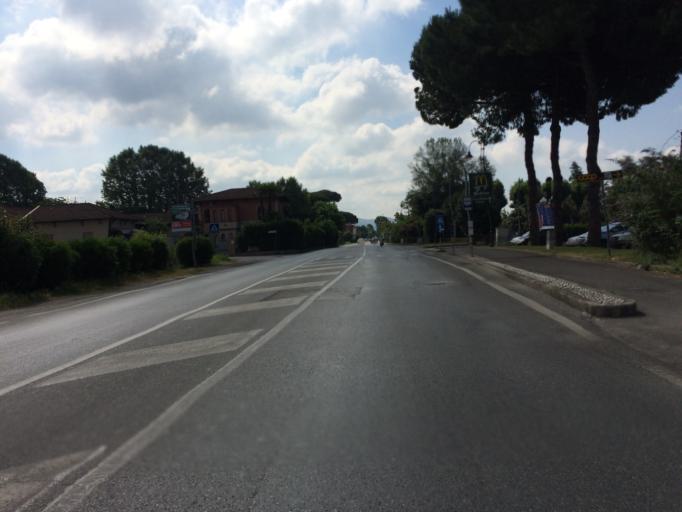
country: IT
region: Tuscany
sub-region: Provincia di Lucca
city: Pietrasanta
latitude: 43.9578
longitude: 10.2250
